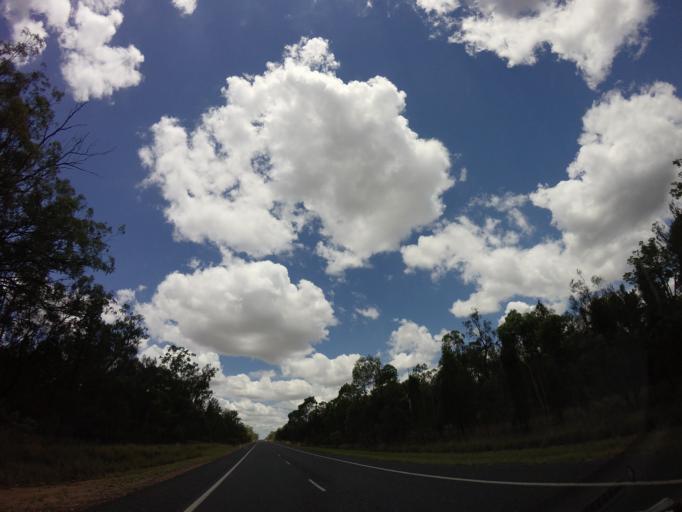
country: AU
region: Queensland
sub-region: Western Downs
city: Dalby
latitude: -27.9758
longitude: 151.0761
